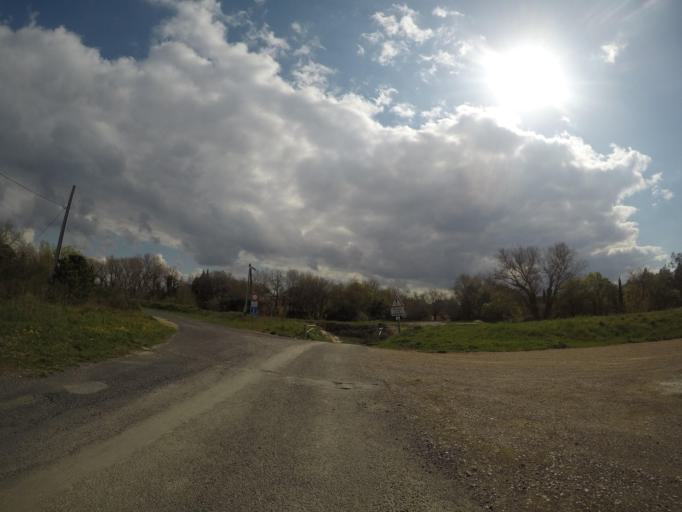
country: FR
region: Languedoc-Roussillon
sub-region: Departement des Pyrenees-Orientales
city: Pezilla-la-Riviere
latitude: 42.6713
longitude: 2.7659
